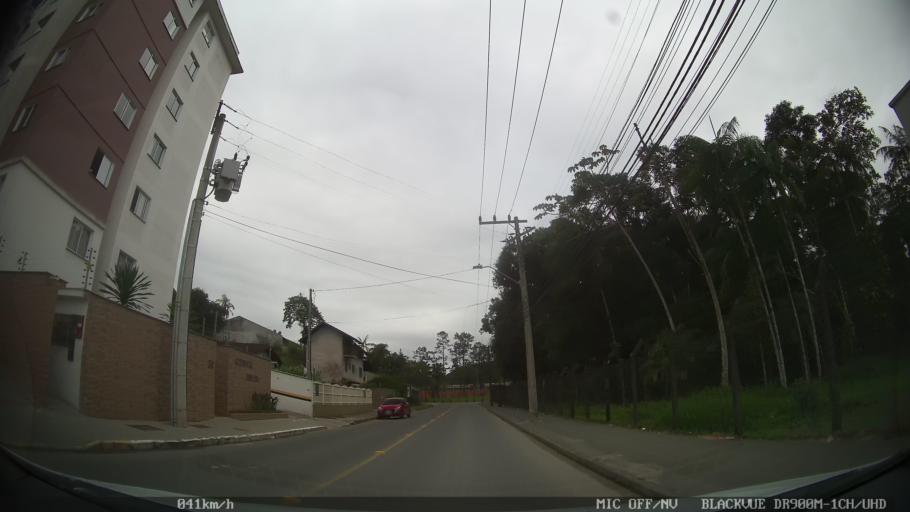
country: BR
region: Santa Catarina
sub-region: Joinville
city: Joinville
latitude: -26.2656
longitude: -48.8897
